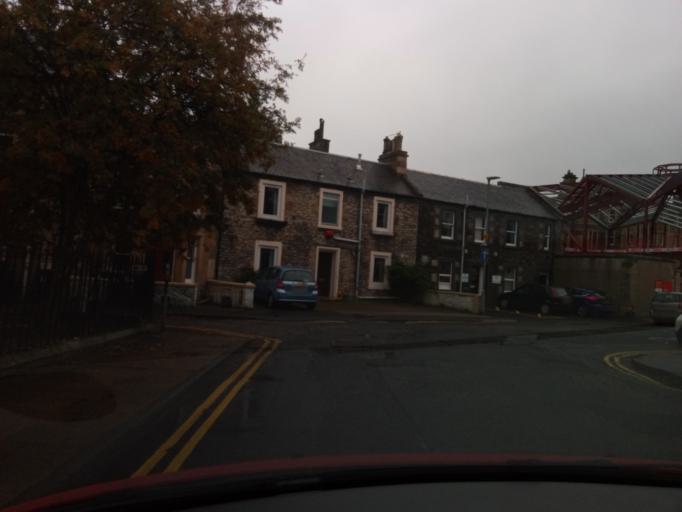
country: GB
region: Scotland
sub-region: The Scottish Borders
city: Galashiels
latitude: 55.6180
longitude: -2.8097
